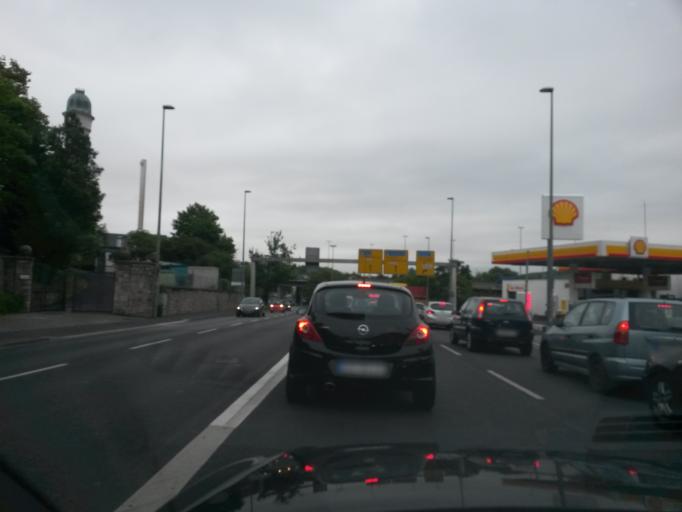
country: DE
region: Bavaria
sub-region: Regierungsbezirk Unterfranken
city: Wuerzburg
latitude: 49.7997
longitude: 9.9562
